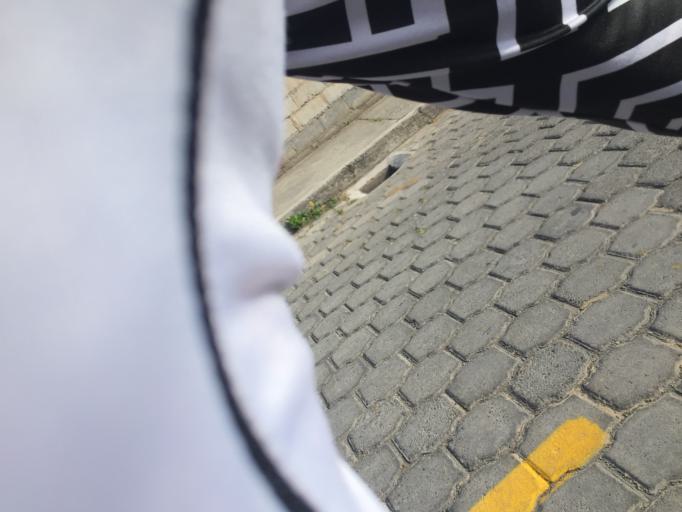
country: EC
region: Imbabura
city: Atuntaqui
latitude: 0.3392
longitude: -78.1901
